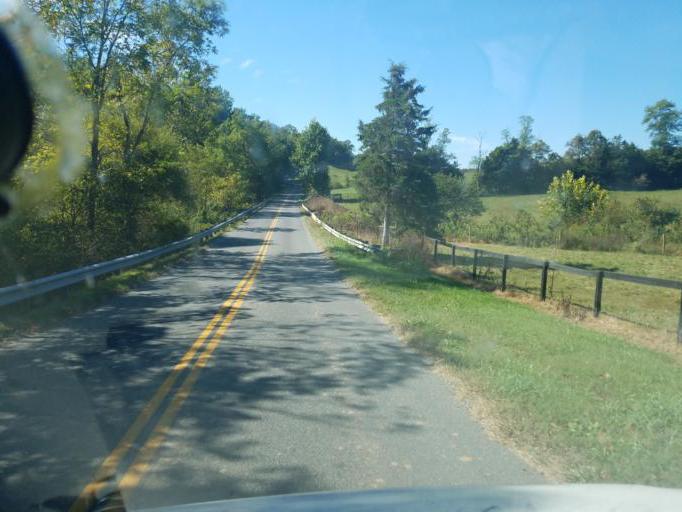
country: US
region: Virginia
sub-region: Greene County
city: Stanardsville
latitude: 38.3503
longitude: -78.4244
